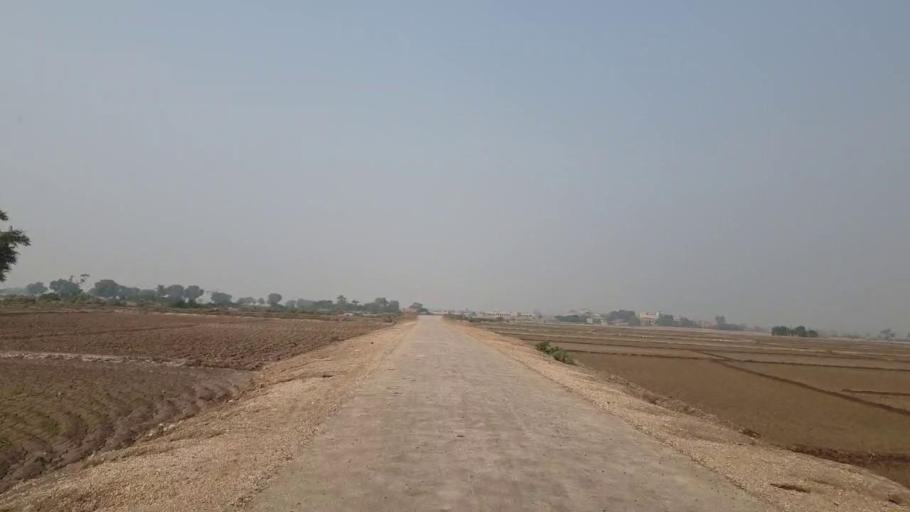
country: PK
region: Sindh
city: Bhan
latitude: 26.5016
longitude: 67.6939
